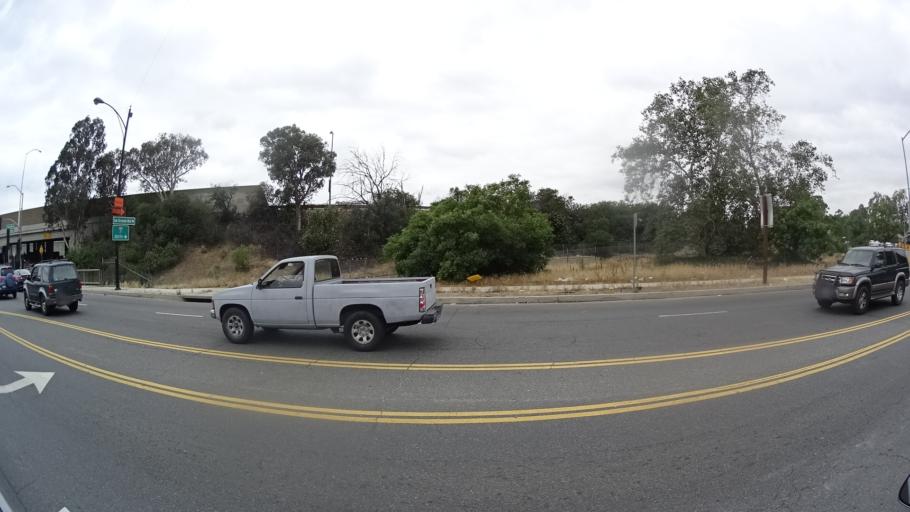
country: US
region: California
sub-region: Los Angeles County
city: Burbank
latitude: 34.2001
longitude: -118.3376
